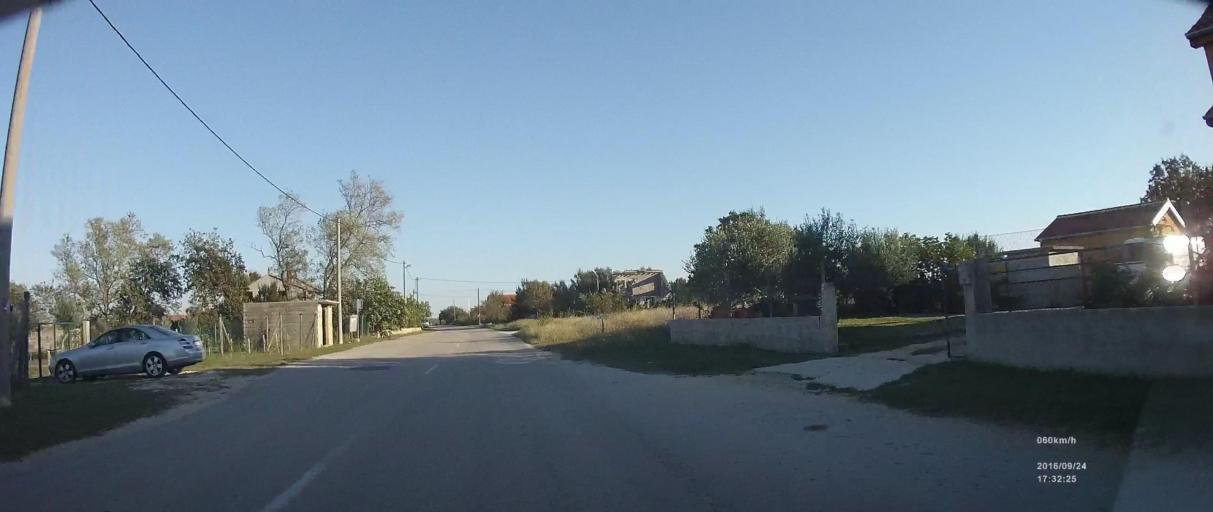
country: HR
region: Zadarska
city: Posedarje
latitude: 44.1824
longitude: 15.4501
